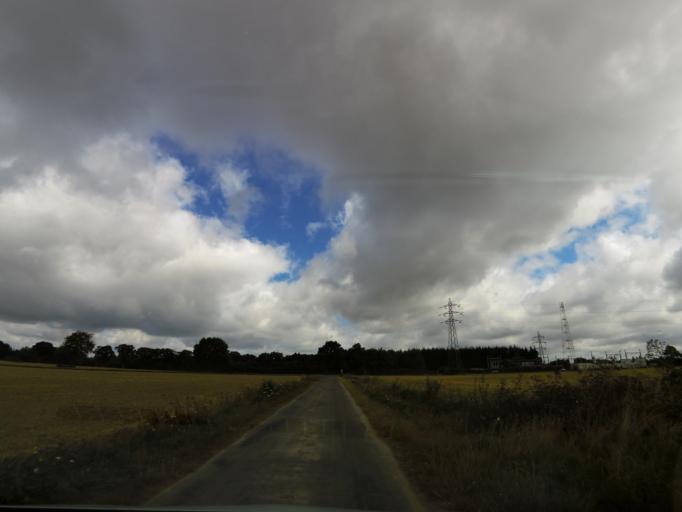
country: FR
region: Brittany
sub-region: Departement d'Ille-et-Vilaine
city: Crevin
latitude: 47.9373
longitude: -1.6426
